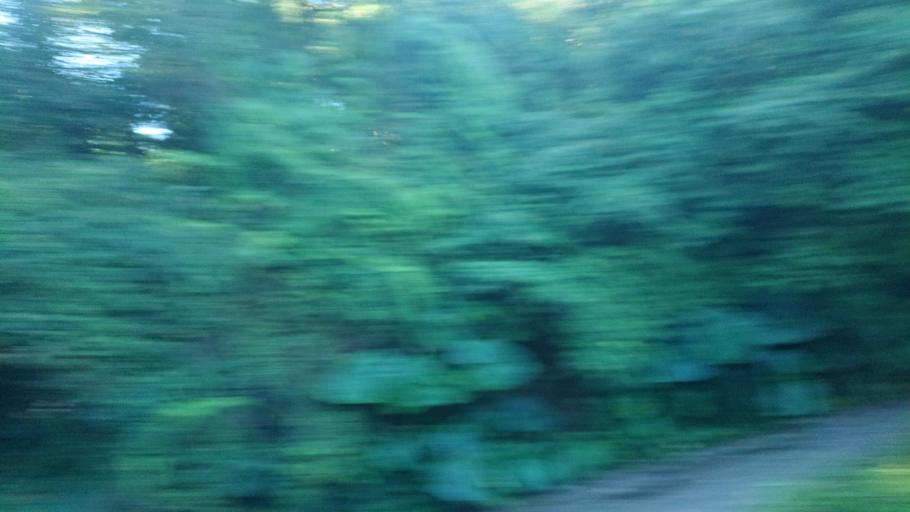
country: TW
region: Taiwan
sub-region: Chiayi
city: Jiayi Shi
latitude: 23.5347
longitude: 120.6364
